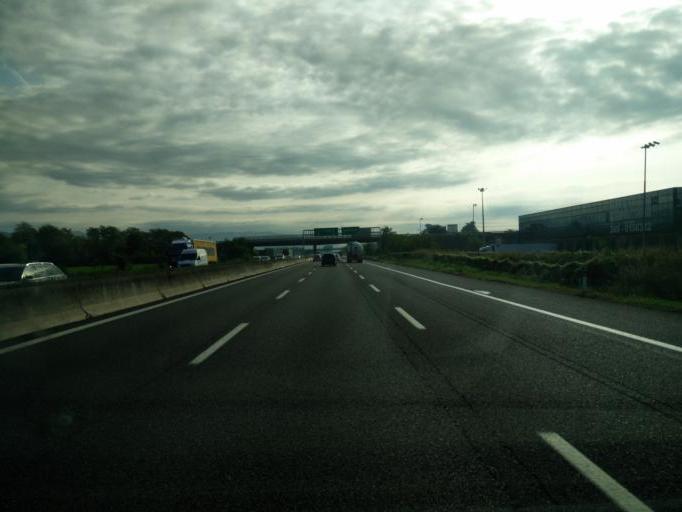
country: IT
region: Lombardy
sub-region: Provincia di Brescia
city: Ospitaletto
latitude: 45.5666
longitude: 10.0628
